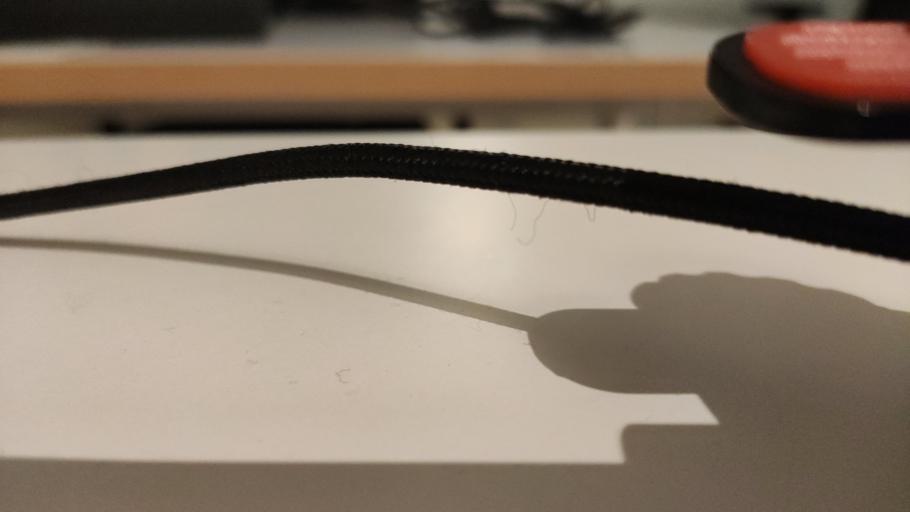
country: RU
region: Moskovskaya
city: Ol'yavidovo
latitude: 56.4218
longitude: 37.7421
